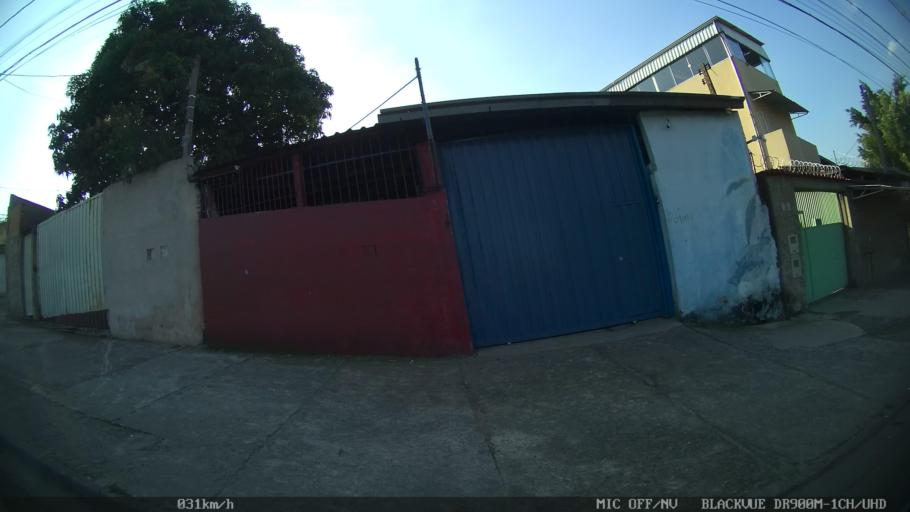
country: BR
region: Sao Paulo
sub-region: Campinas
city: Campinas
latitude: -22.9827
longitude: -47.1454
